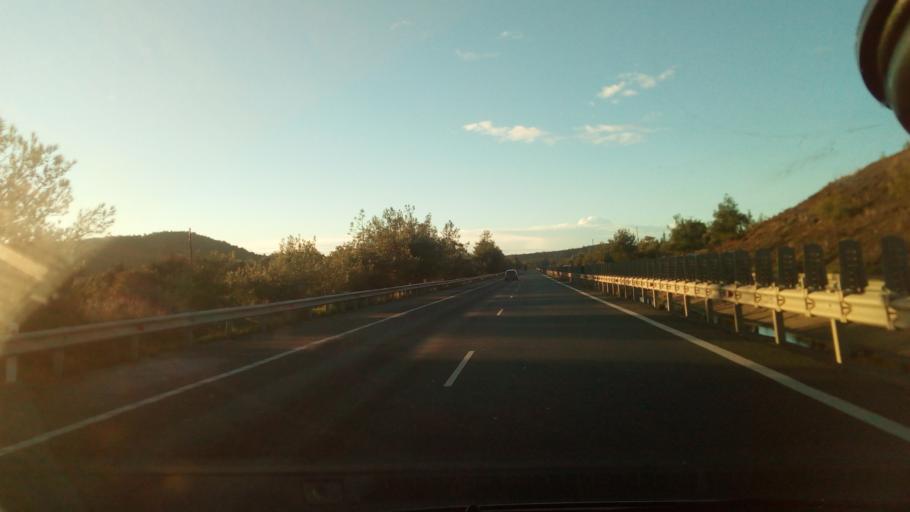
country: CY
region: Larnaka
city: Kofinou
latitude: 34.8660
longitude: 33.3950
